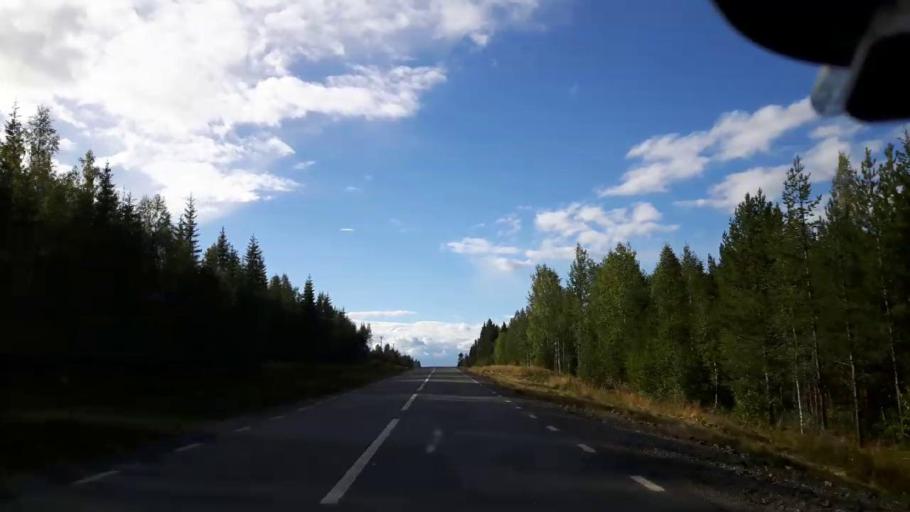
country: SE
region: Jaemtland
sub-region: Stroemsunds Kommun
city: Stroemsund
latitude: 63.5747
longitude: 15.7544
